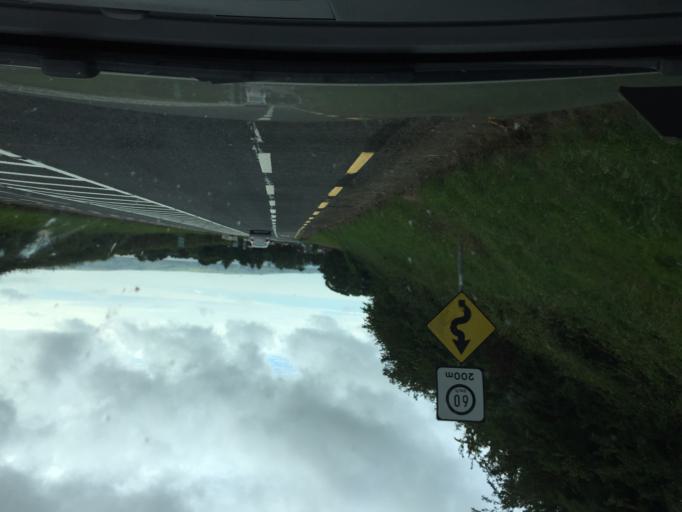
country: IE
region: Munster
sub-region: Waterford
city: Dungarvan
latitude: 52.1236
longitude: -7.5638
